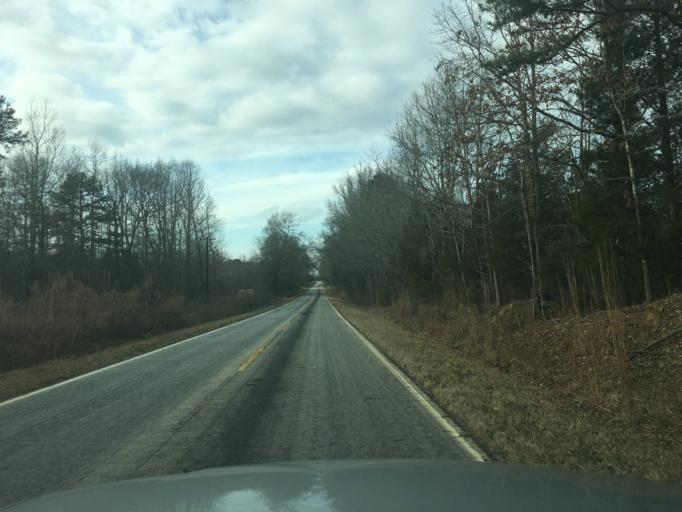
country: US
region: South Carolina
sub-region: Abbeville County
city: Due West
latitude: 34.3491
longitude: -82.4998
